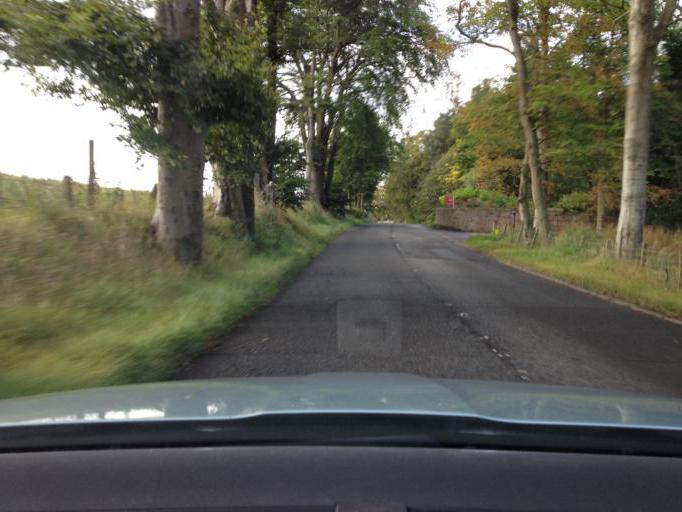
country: GB
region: Scotland
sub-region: West Lothian
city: West Calder
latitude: 55.8341
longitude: -3.5363
